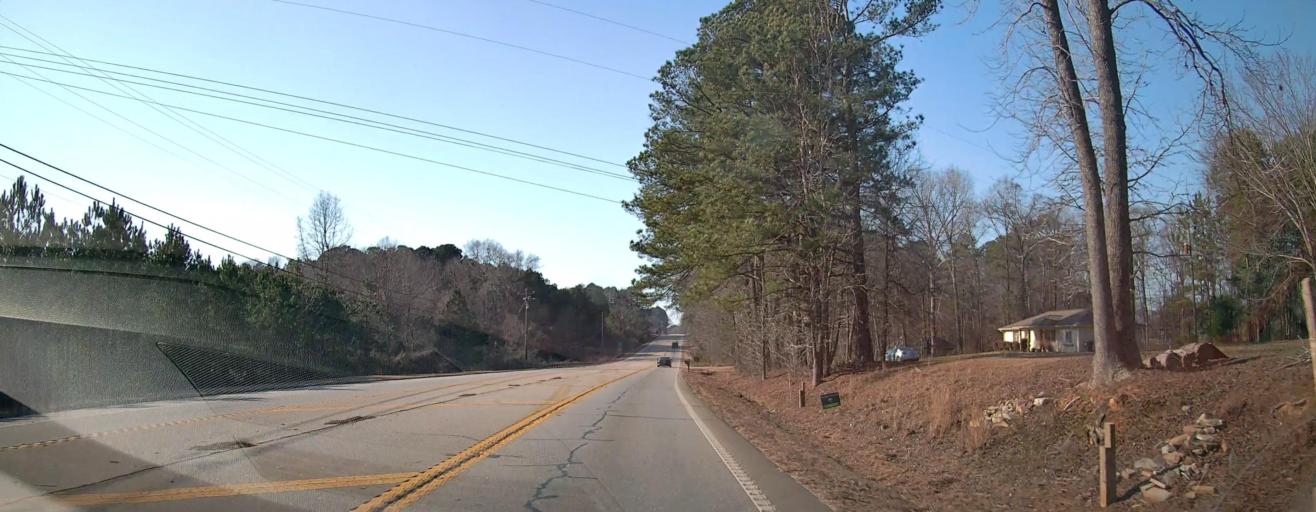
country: US
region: Georgia
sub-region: Henry County
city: Locust Grove
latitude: 33.3353
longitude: -84.0905
